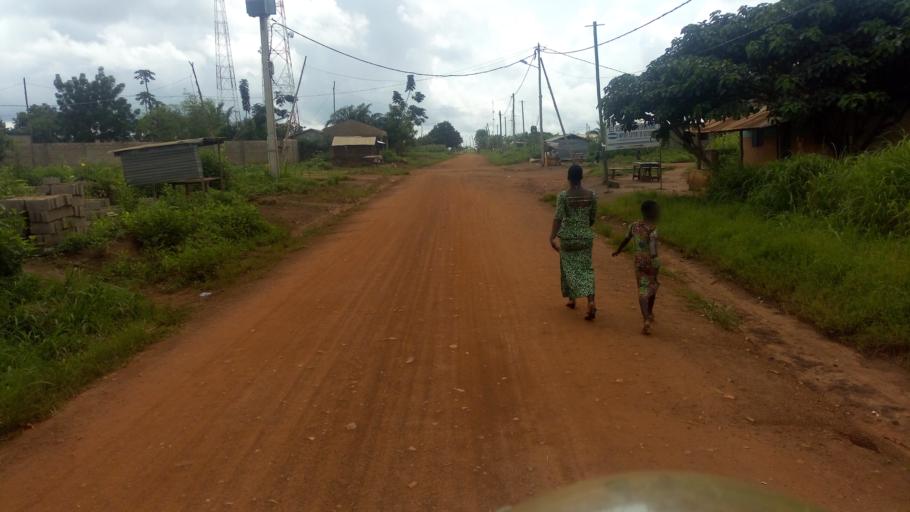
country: TG
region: Centrale
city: Sotouboua
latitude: 8.5556
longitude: 1.0022
